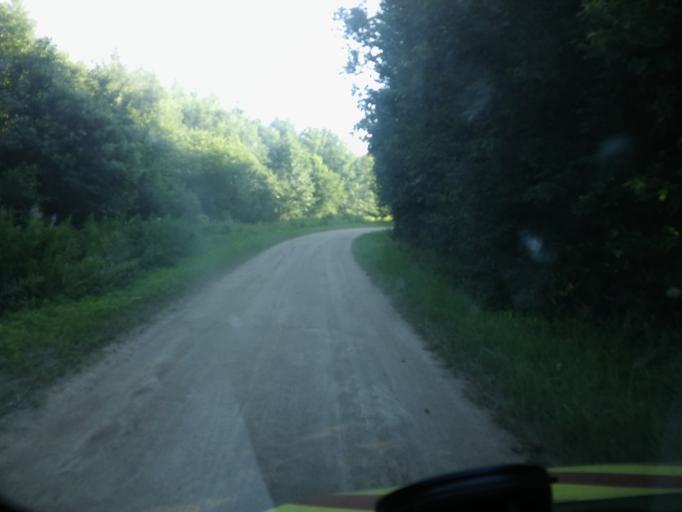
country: EE
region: Valgamaa
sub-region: Torva linn
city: Torva
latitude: 58.0962
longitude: 25.9997
